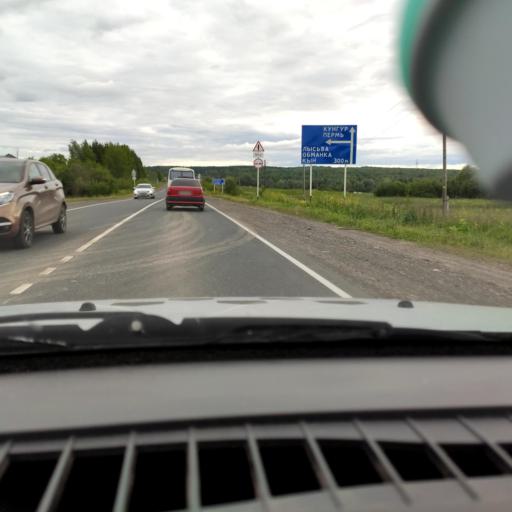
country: RU
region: Perm
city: Lys'va
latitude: 58.1666
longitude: 57.7789
